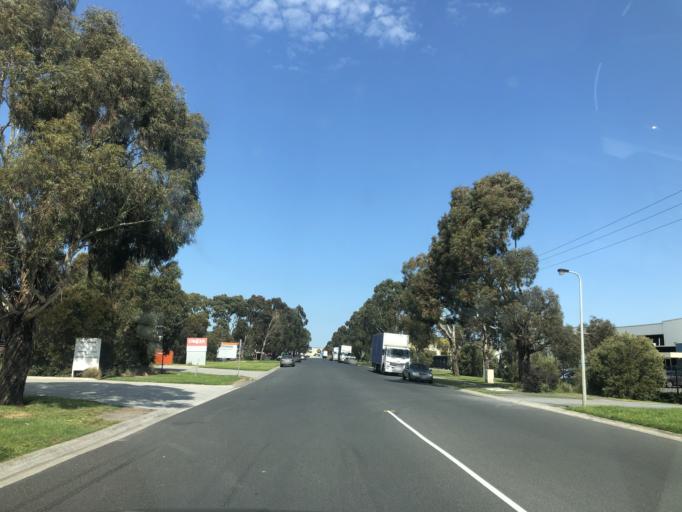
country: AU
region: Victoria
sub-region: Casey
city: Hampton Park
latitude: -38.0367
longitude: 145.2413
